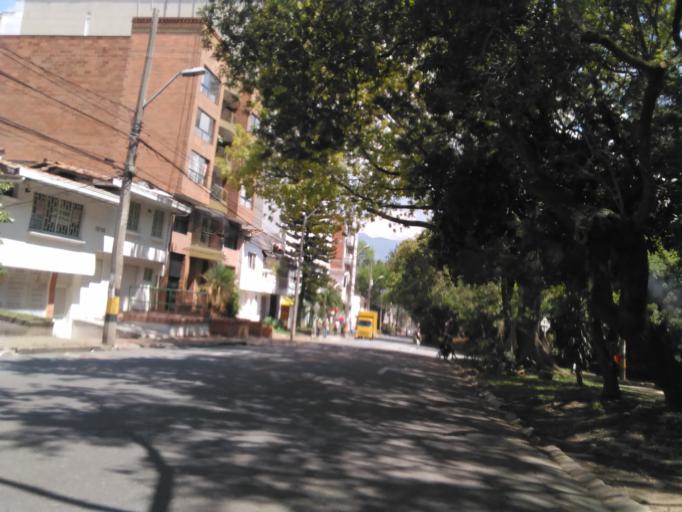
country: CO
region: Antioquia
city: Medellin
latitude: 6.2385
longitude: -75.5947
